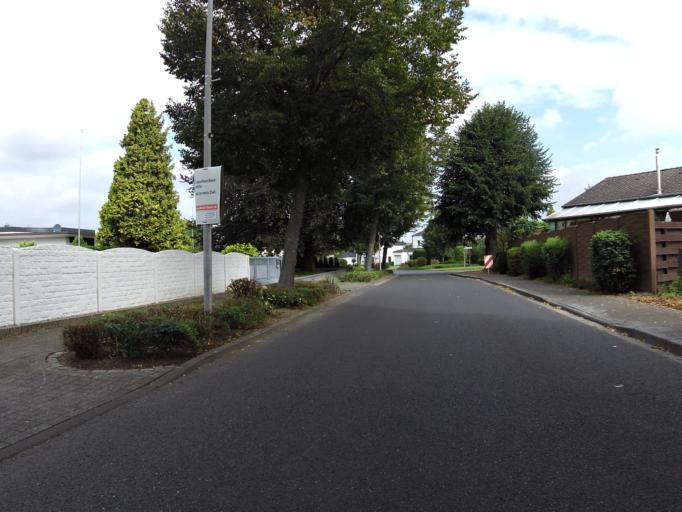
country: DE
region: North Rhine-Westphalia
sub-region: Regierungsbezirk Koln
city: Ubach-Palenberg
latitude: 50.9490
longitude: 6.0825
